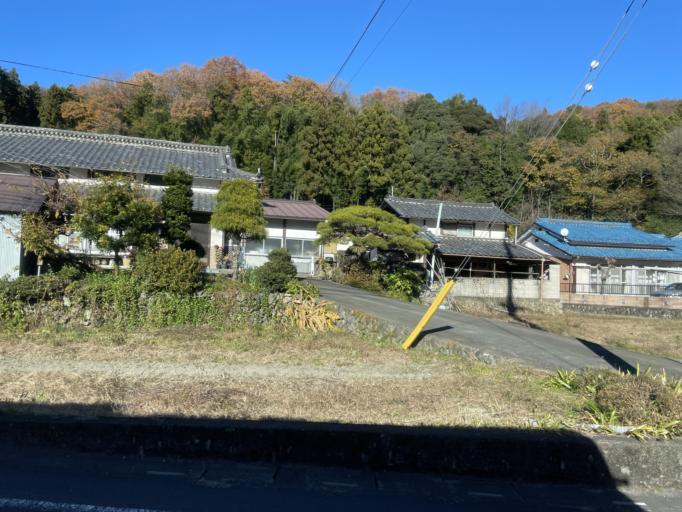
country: JP
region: Saitama
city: Yorii
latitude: 36.0613
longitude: 139.1920
